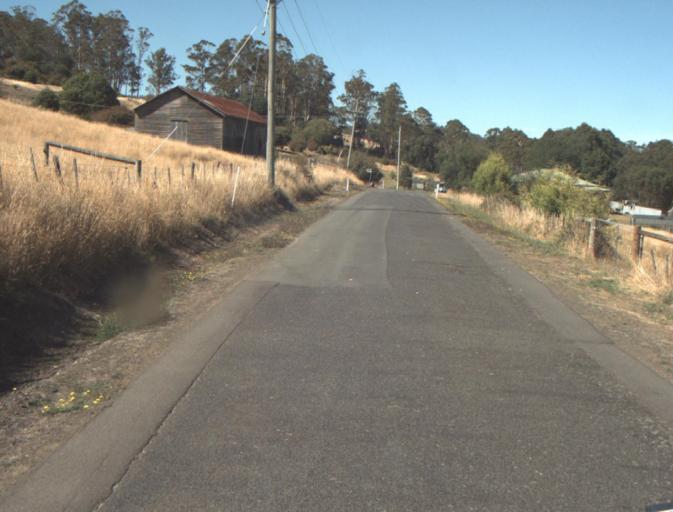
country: AU
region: Tasmania
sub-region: Launceston
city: Newstead
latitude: -41.3525
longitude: 147.3038
